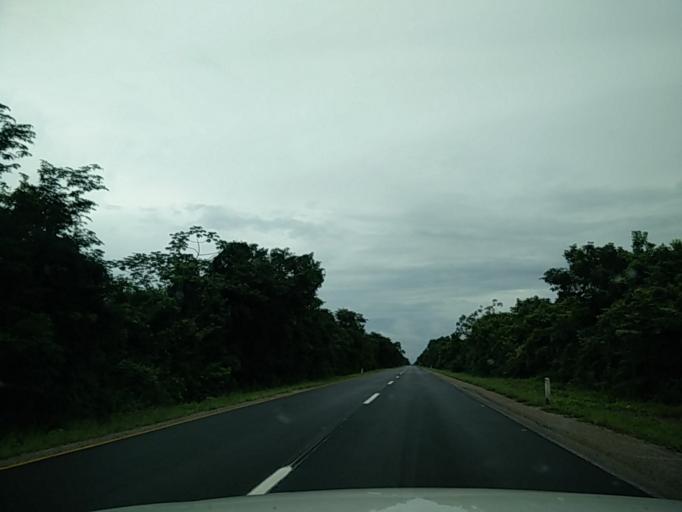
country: MX
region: Quintana Roo
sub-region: Lazaro Cardenas
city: Nuevo Xcan
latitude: 20.8810
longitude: -87.5896
